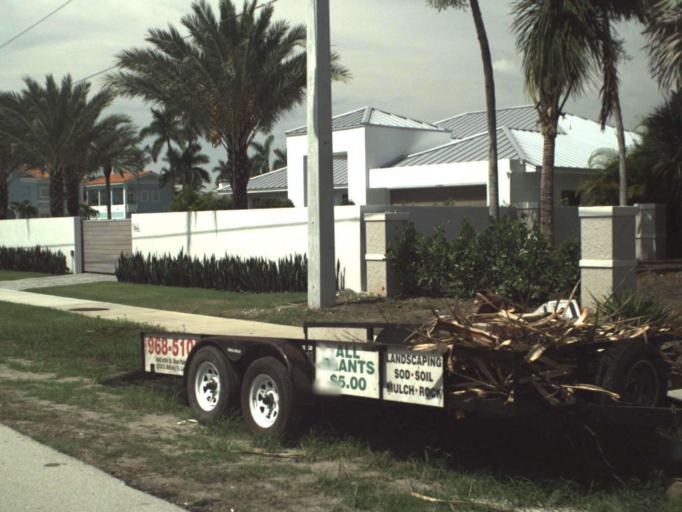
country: US
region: Florida
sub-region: Palm Beach County
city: Delray Beach
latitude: 26.4481
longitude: -80.0613
